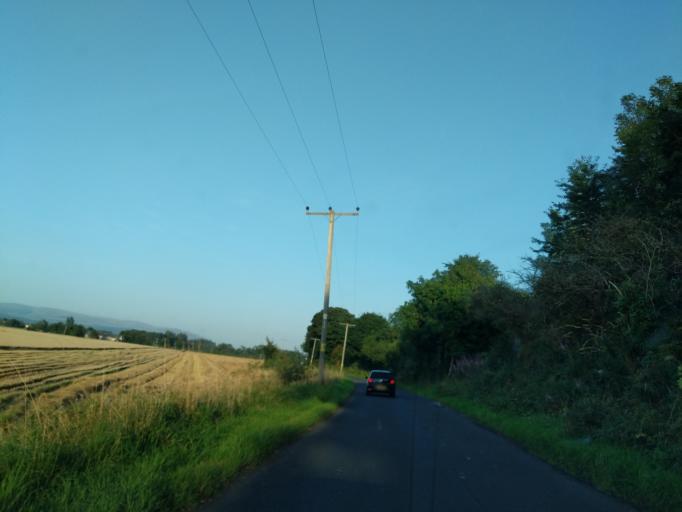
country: GB
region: Scotland
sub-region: Stirling
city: Doune
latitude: 56.1272
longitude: -4.0913
